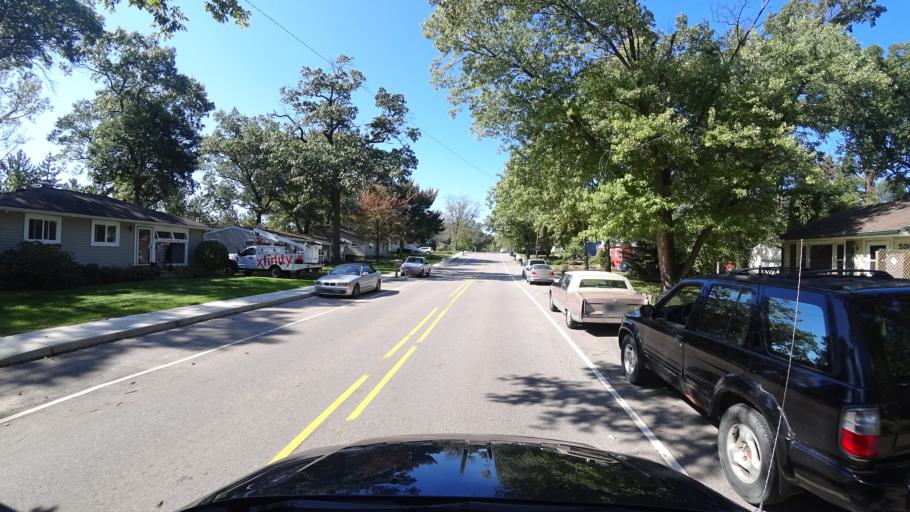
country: US
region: Indiana
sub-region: LaPorte County
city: Michigan City
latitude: 41.7267
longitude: -86.8854
